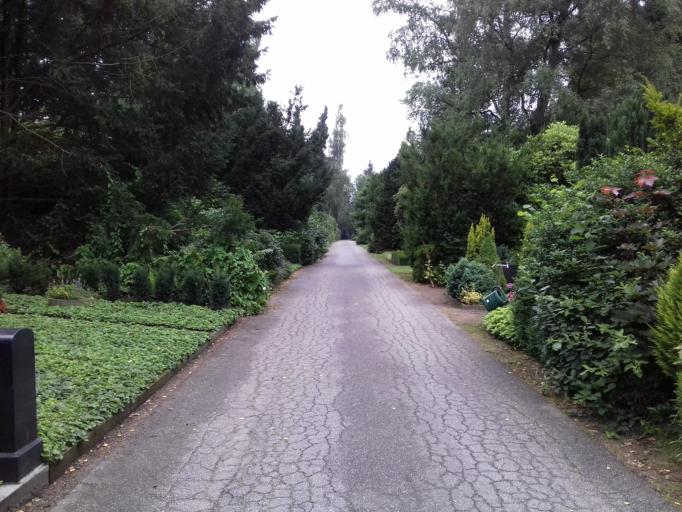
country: DE
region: Schleswig-Holstein
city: Neumunster
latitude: 54.0720
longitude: 10.0039
